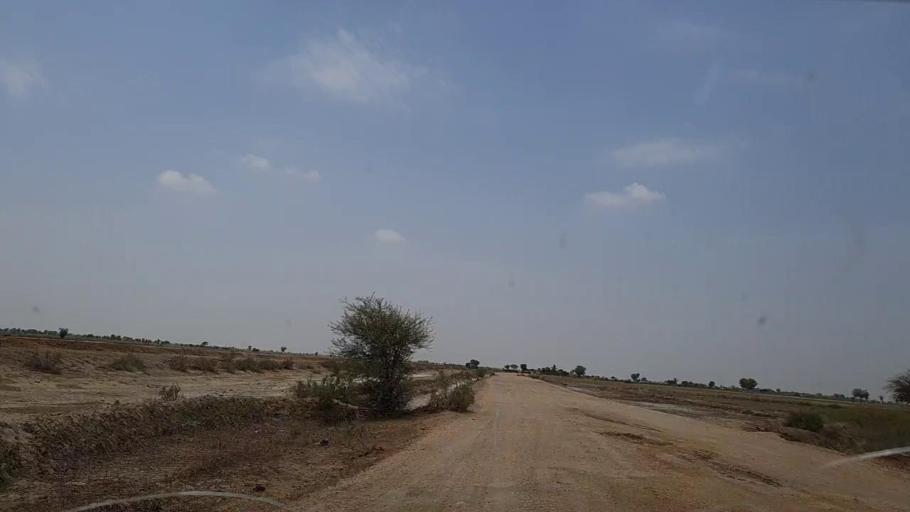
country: PK
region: Sindh
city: Phulji
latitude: 26.8002
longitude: 67.6362
